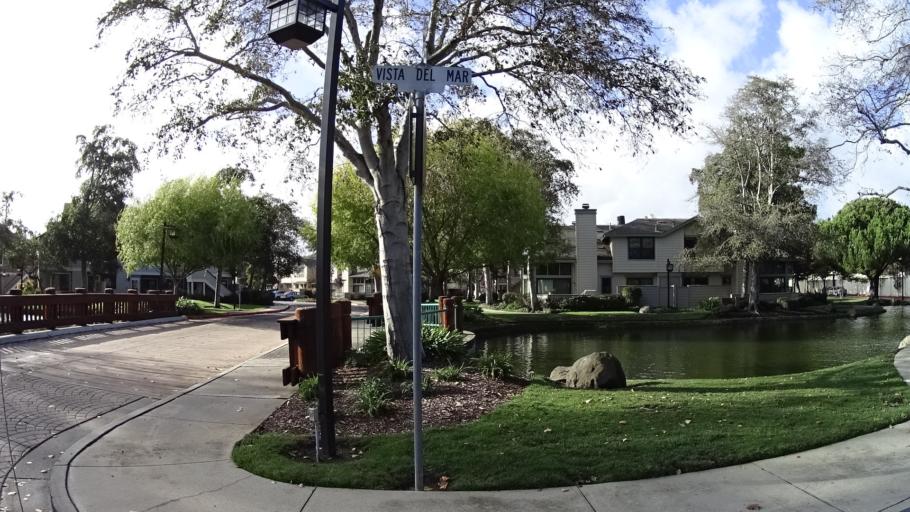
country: US
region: California
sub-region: San Mateo County
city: Foster City
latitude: 37.5547
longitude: -122.2834
